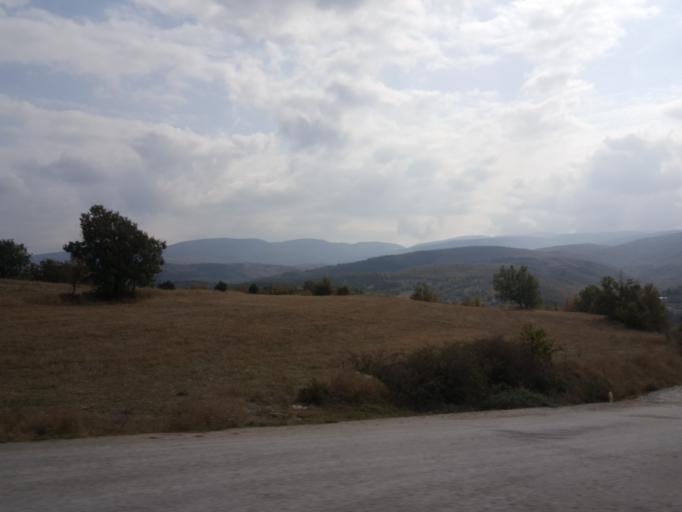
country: TR
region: Sinop
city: Sarayduzu
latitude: 41.3286
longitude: 34.7676
